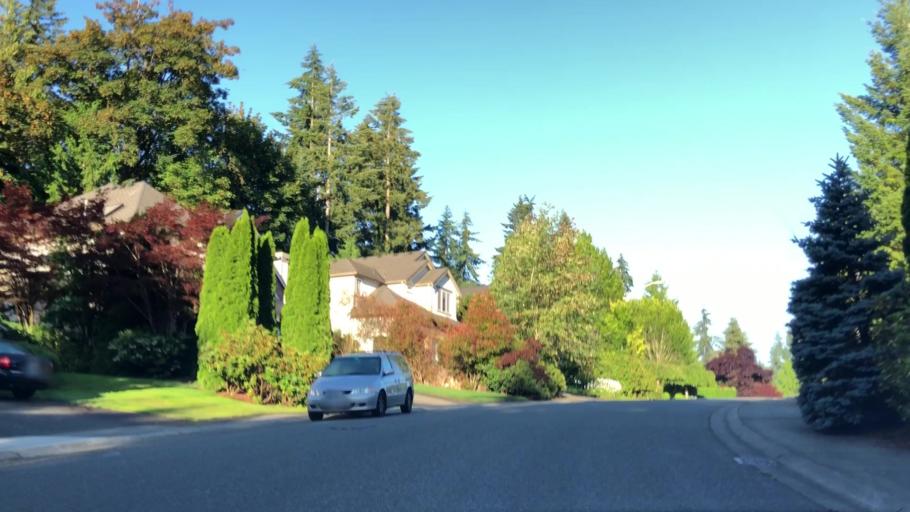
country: US
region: Washington
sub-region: King County
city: Redmond
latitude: 47.6969
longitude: -122.1132
